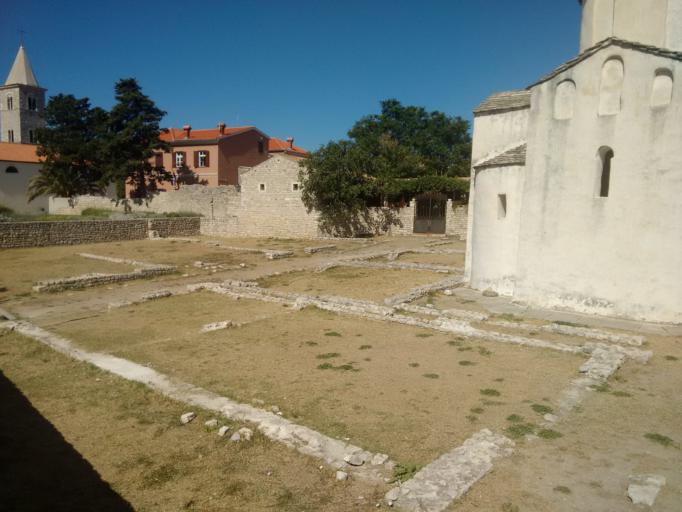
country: HR
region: Zadarska
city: Nin
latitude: 44.2427
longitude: 15.1846
